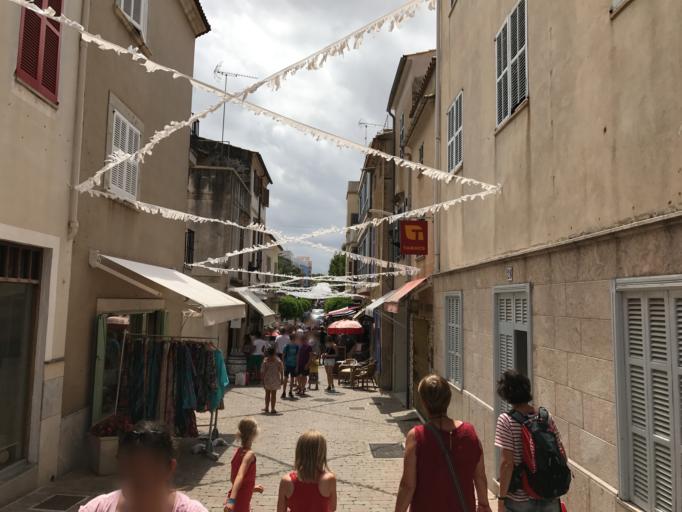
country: ES
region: Balearic Islands
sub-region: Illes Balears
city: Arta
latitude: 39.6939
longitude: 3.3506
